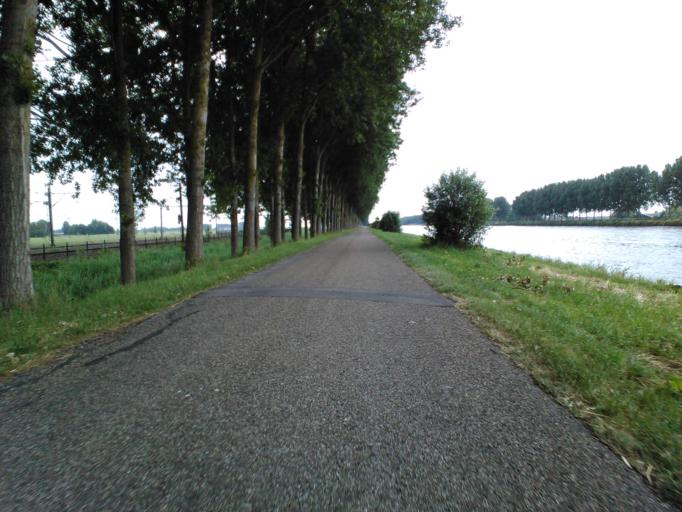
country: NL
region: Utrecht
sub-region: Stichtse Vecht
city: Vreeland
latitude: 52.2346
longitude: 5.0082
